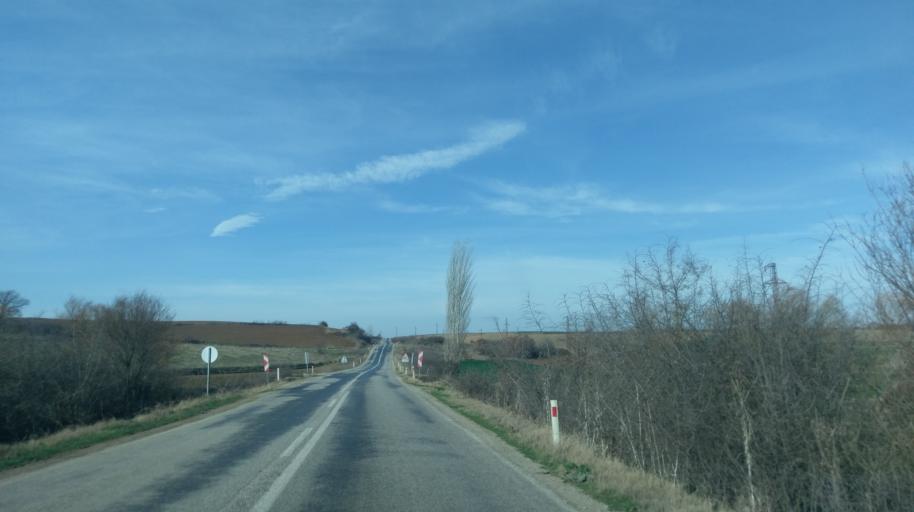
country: TR
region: Edirne
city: Uzun Keupru
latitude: 41.2763
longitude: 26.7523
